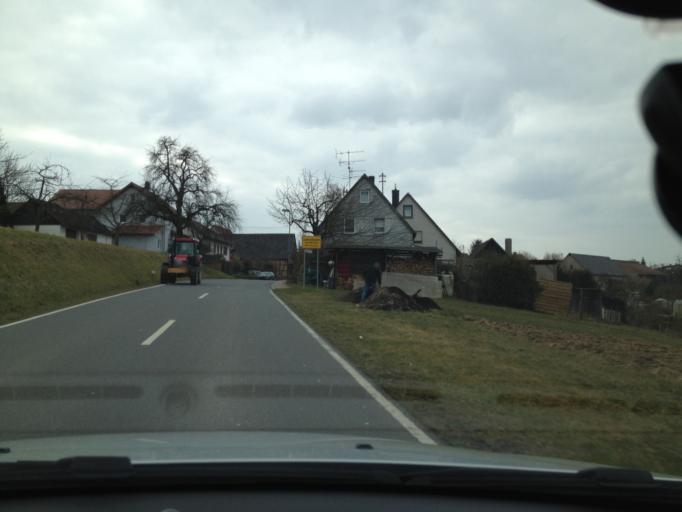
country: DE
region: Baden-Wuerttemberg
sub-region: Regierungsbezirk Stuttgart
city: Wertheim
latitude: 49.7312
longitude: 9.4964
